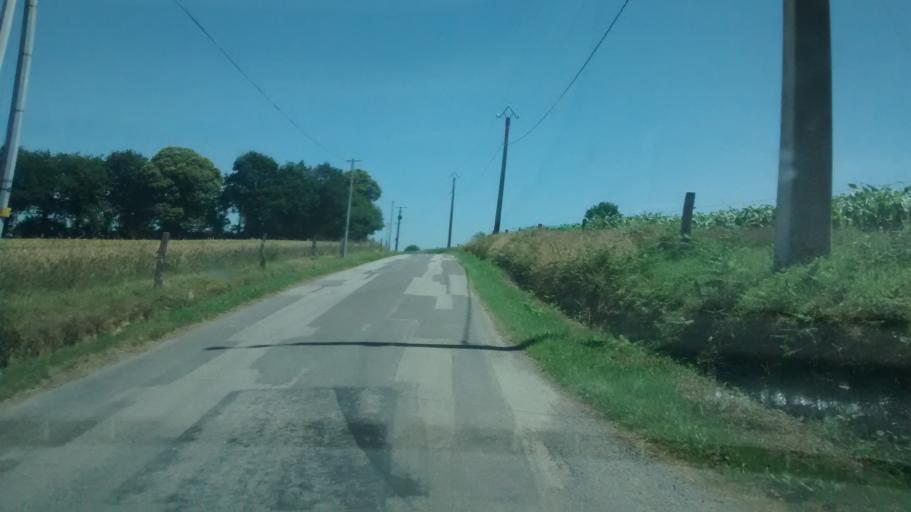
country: FR
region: Brittany
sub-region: Departement du Morbihan
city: Molac
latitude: 47.7197
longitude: -2.4631
